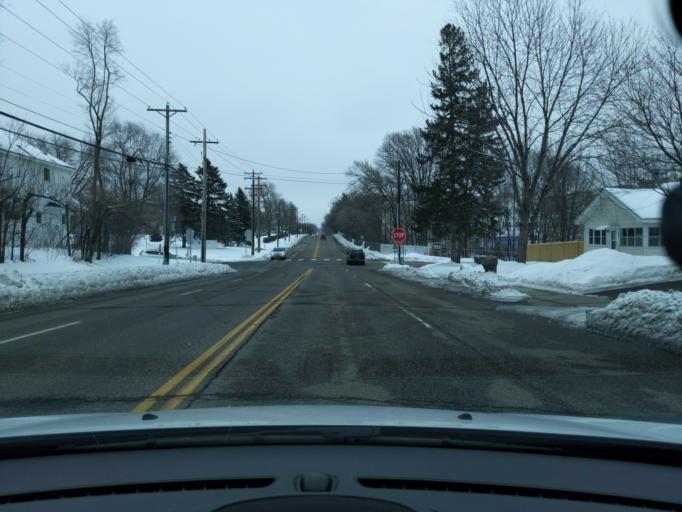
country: US
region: Minnesota
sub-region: Ramsey County
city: Roseville
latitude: 45.0207
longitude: -93.1271
